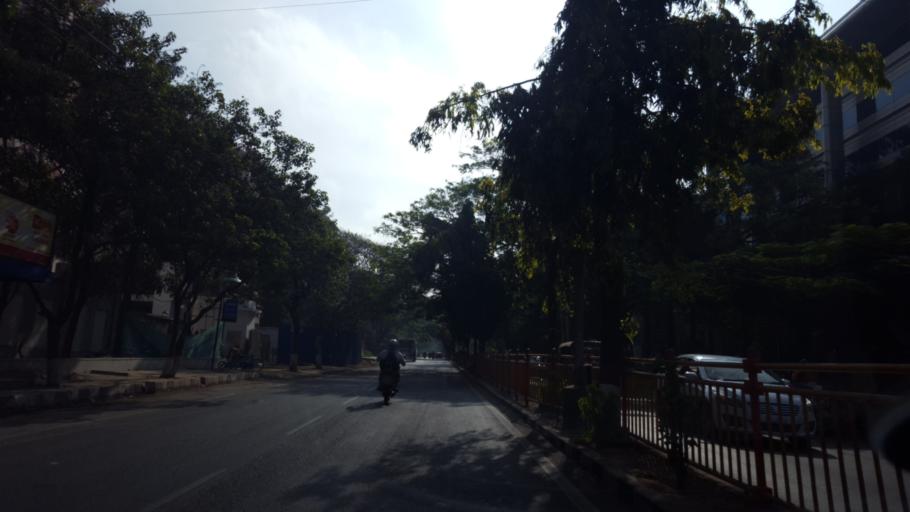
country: IN
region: Karnataka
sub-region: Bangalore Urban
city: Bangalore
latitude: 12.9600
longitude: 77.6472
